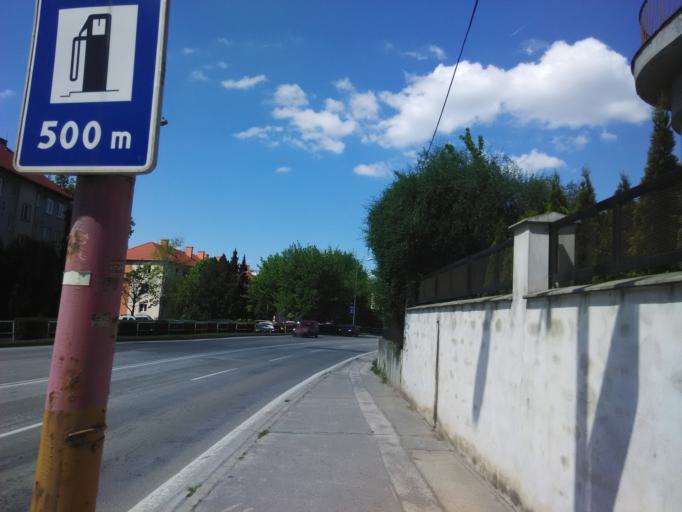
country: SK
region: Trnavsky
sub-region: Okres Trnava
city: Trnava
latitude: 48.3718
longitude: 17.5955
